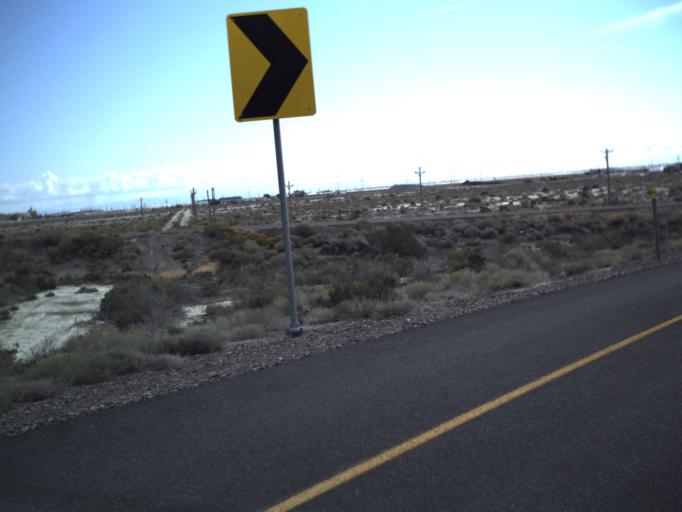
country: US
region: Utah
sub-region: Tooele County
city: Wendover
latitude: 40.7445
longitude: -114.0190
